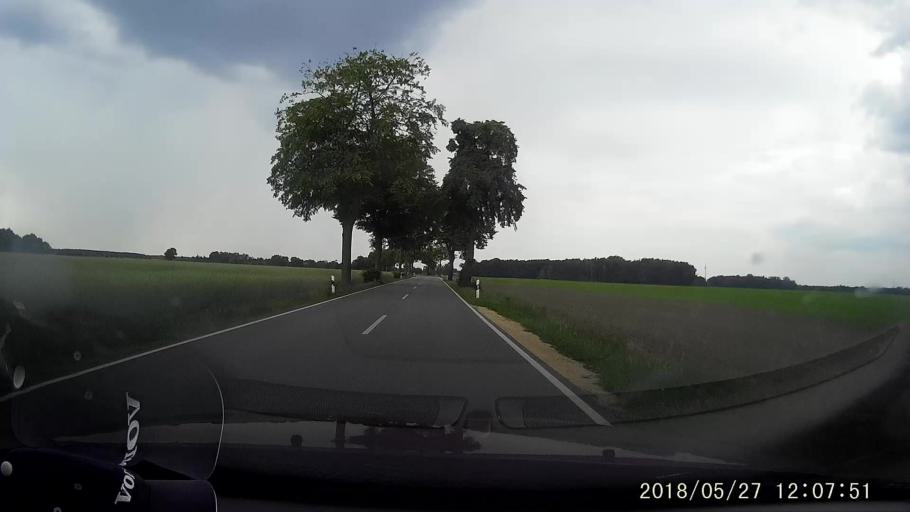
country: DE
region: Saxony
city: Klitten
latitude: 51.3471
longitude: 14.6208
